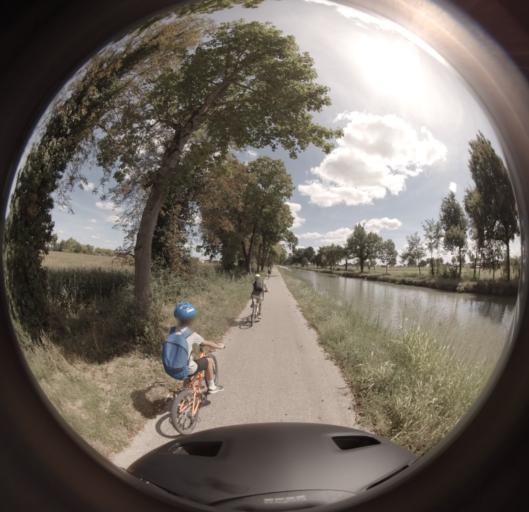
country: FR
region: Midi-Pyrenees
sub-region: Departement du Tarn-et-Garonne
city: Saint-Porquier
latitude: 44.0285
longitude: 1.1461
